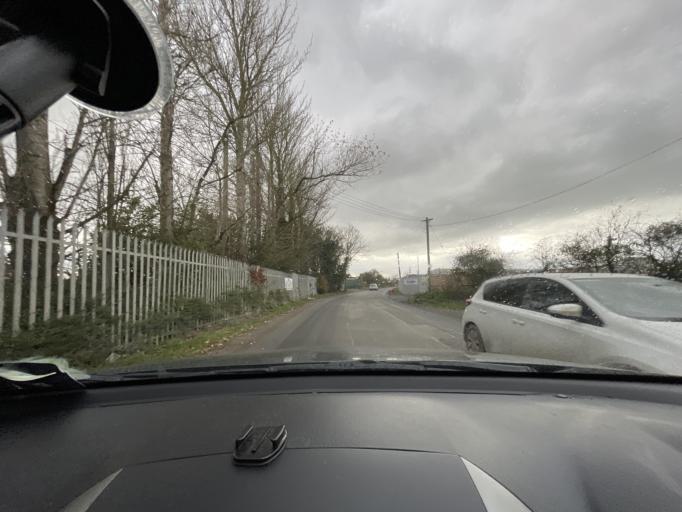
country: IE
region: Leinster
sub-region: Lu
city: Drogheda
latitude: 53.7268
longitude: -6.3188
